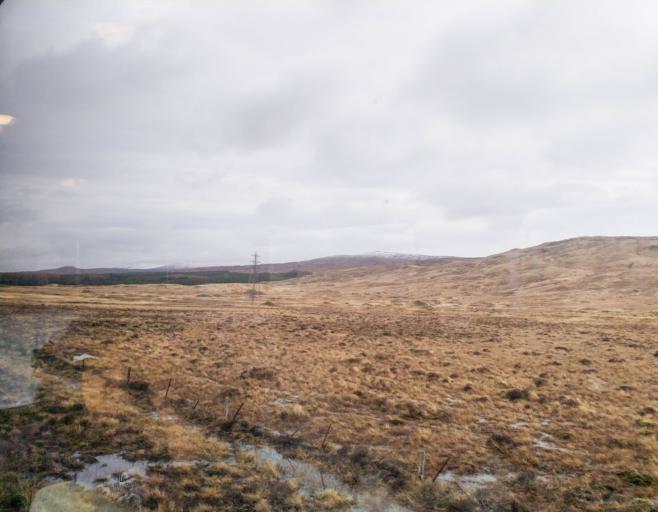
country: GB
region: Scotland
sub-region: Highland
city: Spean Bridge
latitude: 56.5982
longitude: -4.6115
